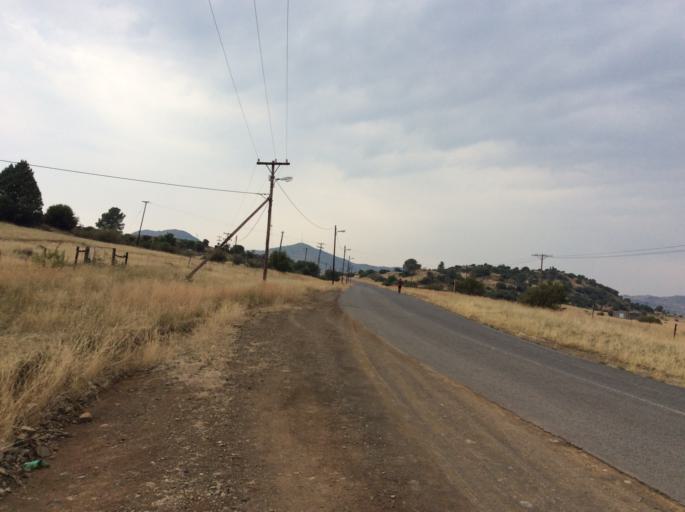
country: LS
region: Mafeteng
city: Mafeteng
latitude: -29.9861
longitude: 27.0193
